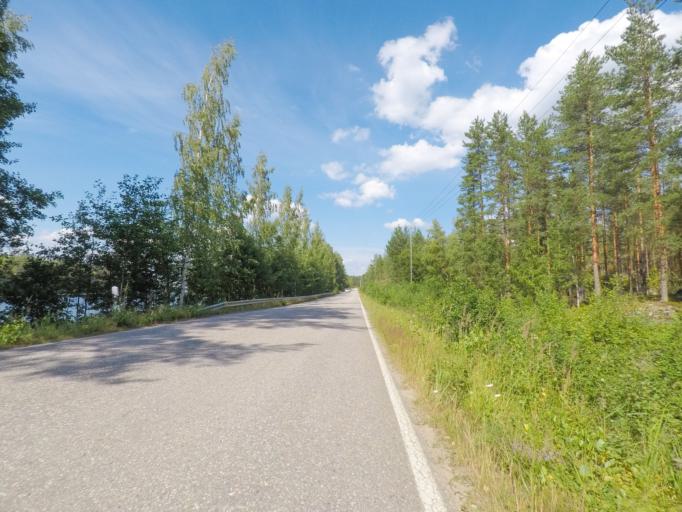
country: FI
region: Southern Savonia
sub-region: Mikkeli
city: Puumala
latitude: 61.4882
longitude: 28.1660
